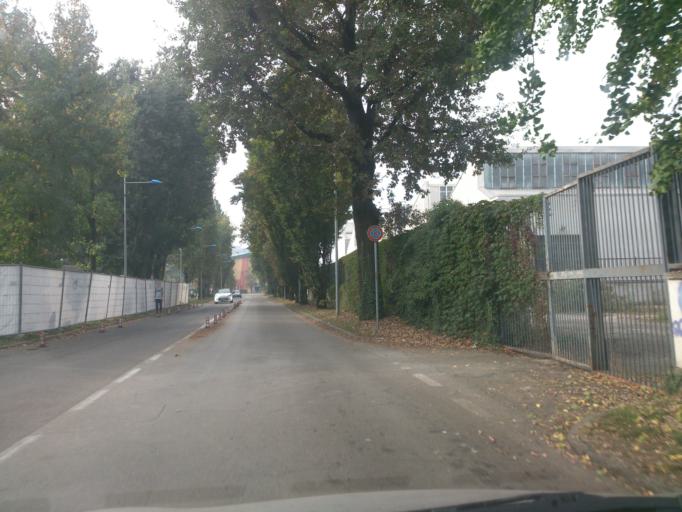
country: IT
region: Lombardy
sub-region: Citta metropolitana di Milano
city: San Donato Milanese
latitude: 45.4225
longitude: 9.2622
